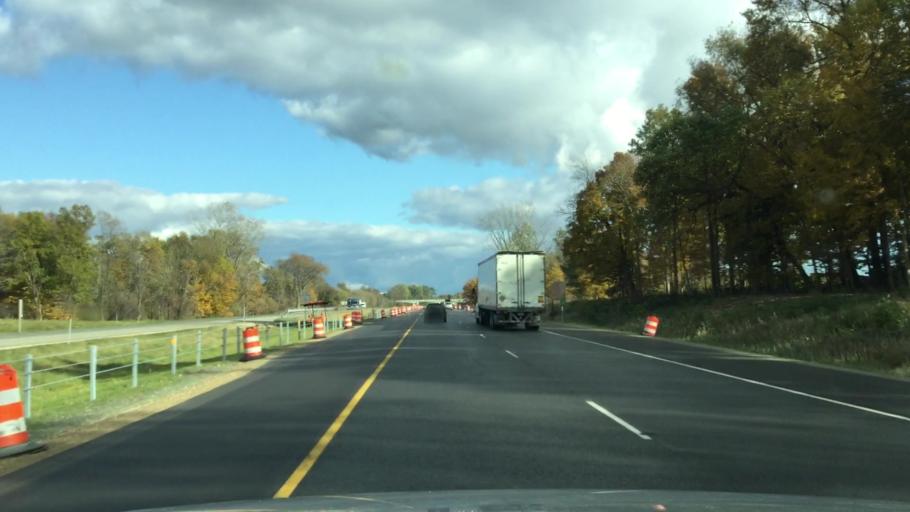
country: US
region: Michigan
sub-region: Van Buren County
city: Decatur
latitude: 42.1963
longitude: -86.0431
